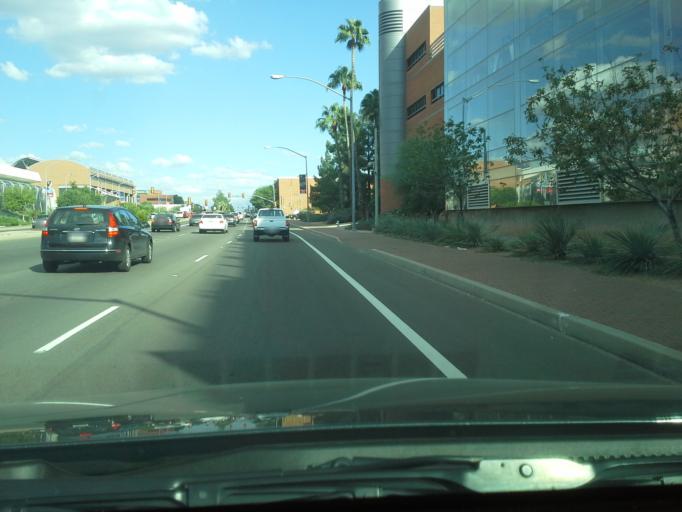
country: US
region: Arizona
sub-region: Pima County
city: Tucson
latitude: 32.2359
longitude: -110.9543
